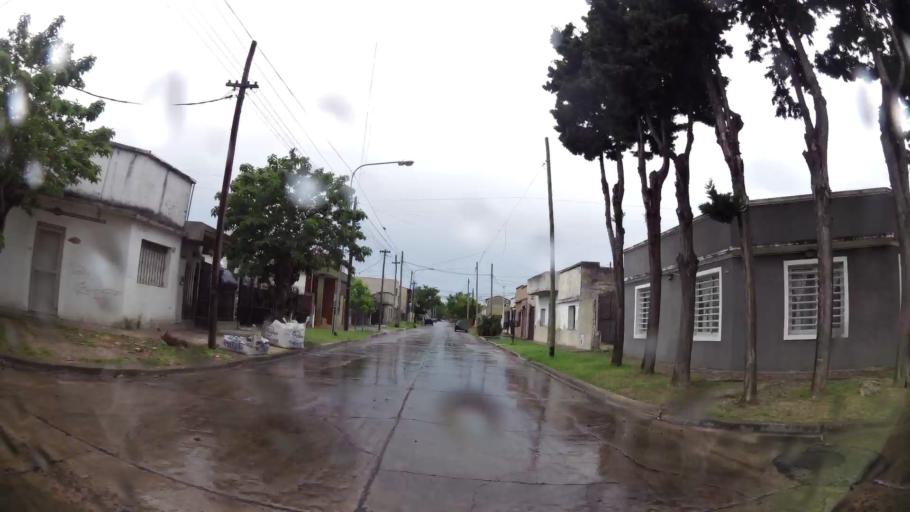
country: AR
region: Buenos Aires
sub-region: Partido de Quilmes
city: Quilmes
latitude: -34.7628
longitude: -58.2218
